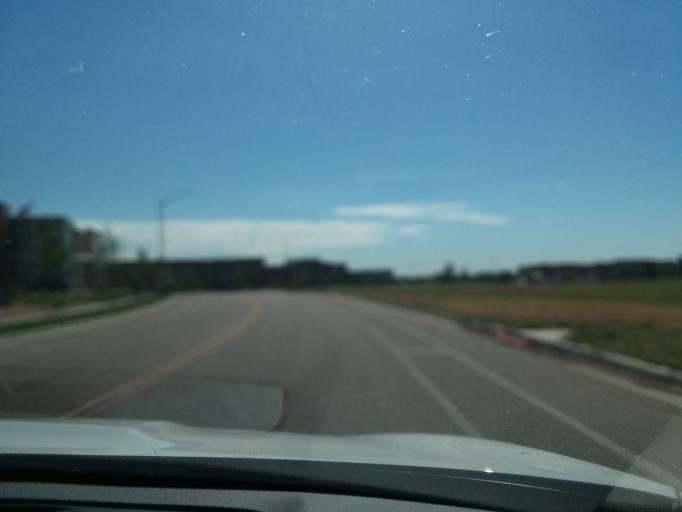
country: US
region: Colorado
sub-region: Larimer County
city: Fort Collins
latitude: 40.5213
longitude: -105.0121
